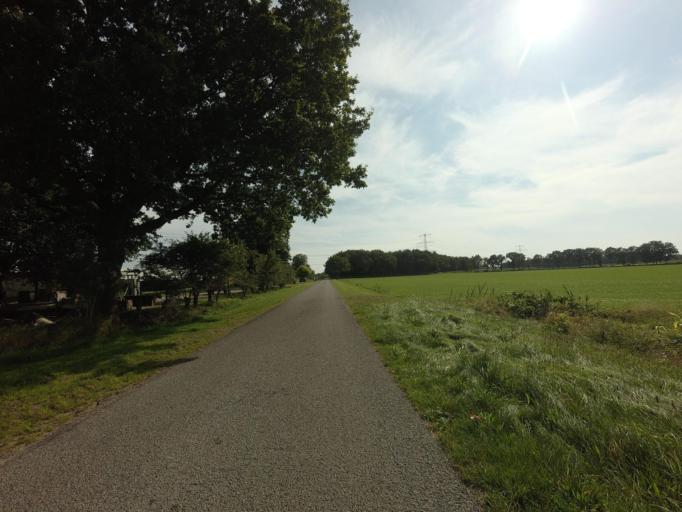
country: NL
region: Drenthe
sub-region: Gemeente Coevorden
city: Dalen
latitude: 52.7310
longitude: 6.7387
